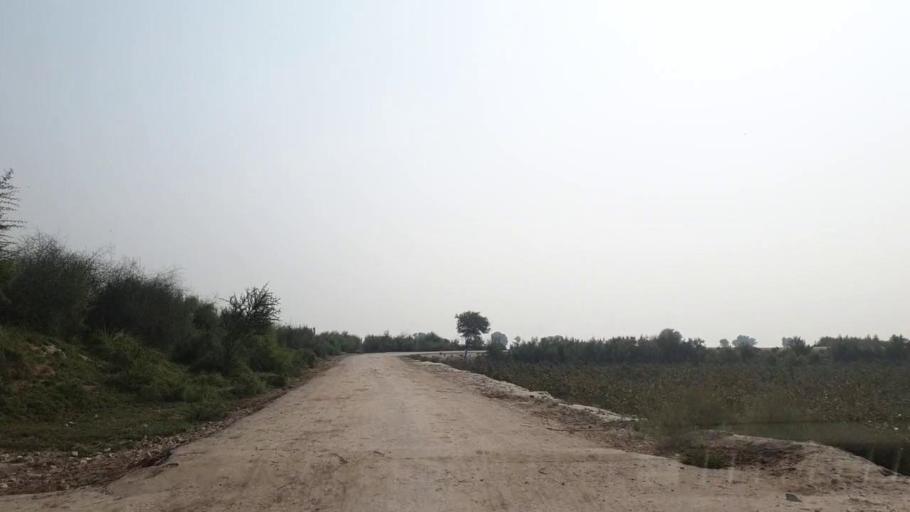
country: PK
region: Sindh
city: Bhan
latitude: 26.5159
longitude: 67.7436
